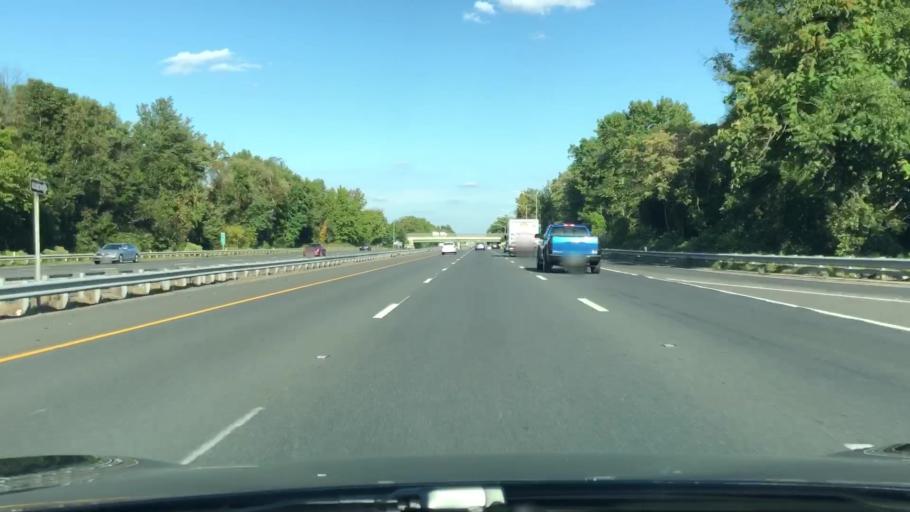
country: US
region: New Jersey
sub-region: Gloucester County
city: Gibbstown
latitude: 39.8106
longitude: -75.2772
